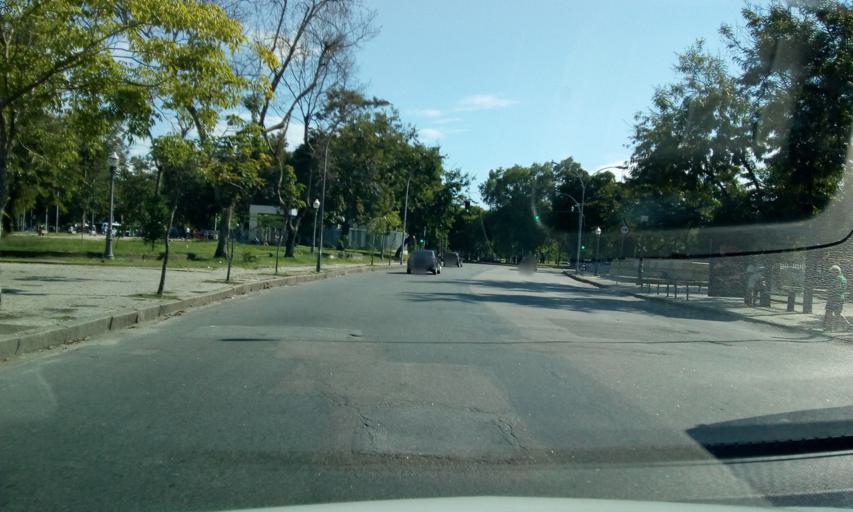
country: BR
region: Rio de Janeiro
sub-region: Rio De Janeiro
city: Rio de Janeiro
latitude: -22.9213
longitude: -43.1767
